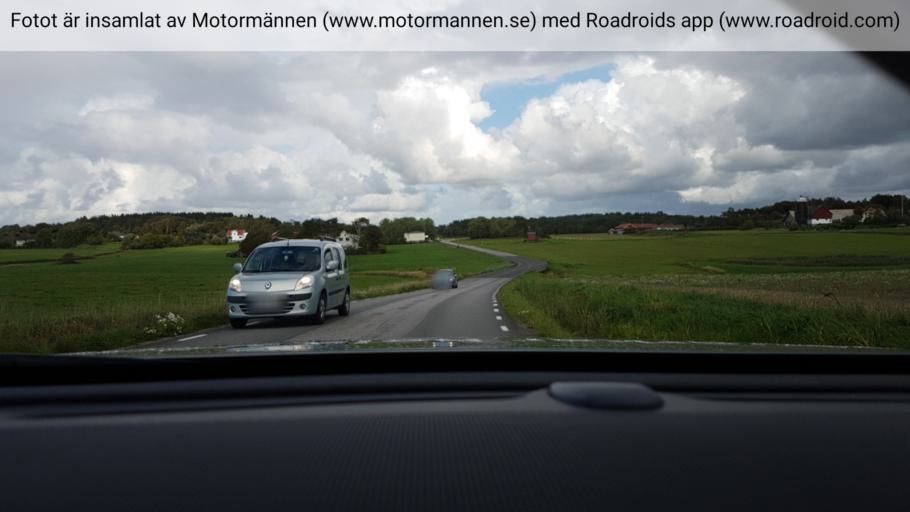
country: SE
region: Vaestra Goetaland
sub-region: Orust
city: Henan
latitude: 58.1516
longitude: 11.5895
